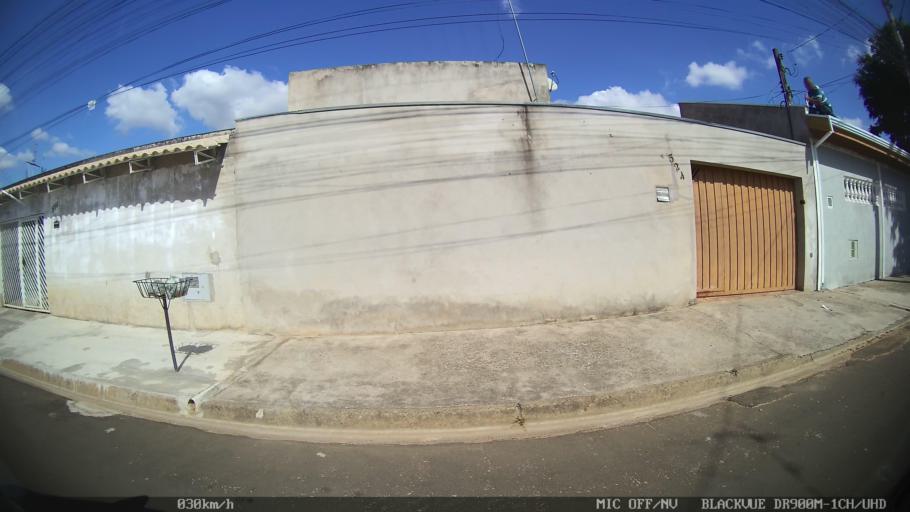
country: BR
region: Sao Paulo
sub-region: Hortolandia
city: Hortolandia
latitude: -22.8921
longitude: -47.2167
